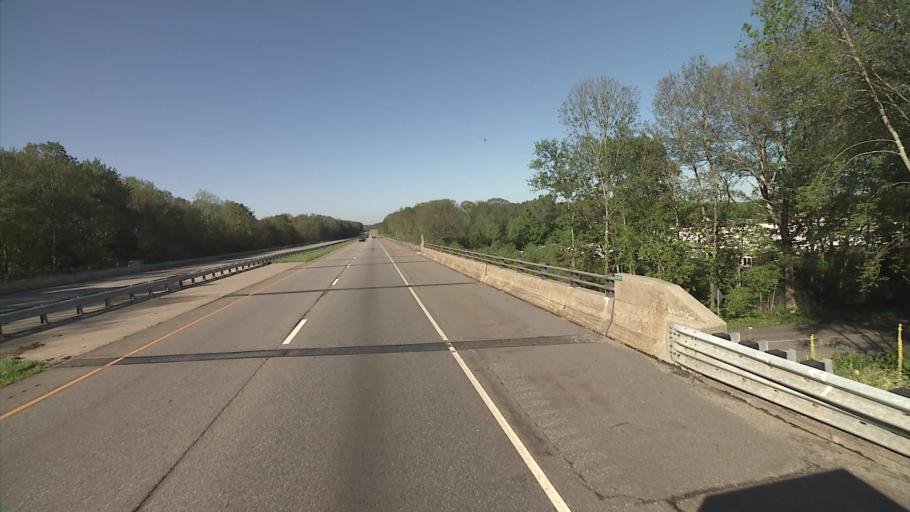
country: US
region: Connecticut
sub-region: Windham County
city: Plainfield Village
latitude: 41.6565
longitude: -71.9239
